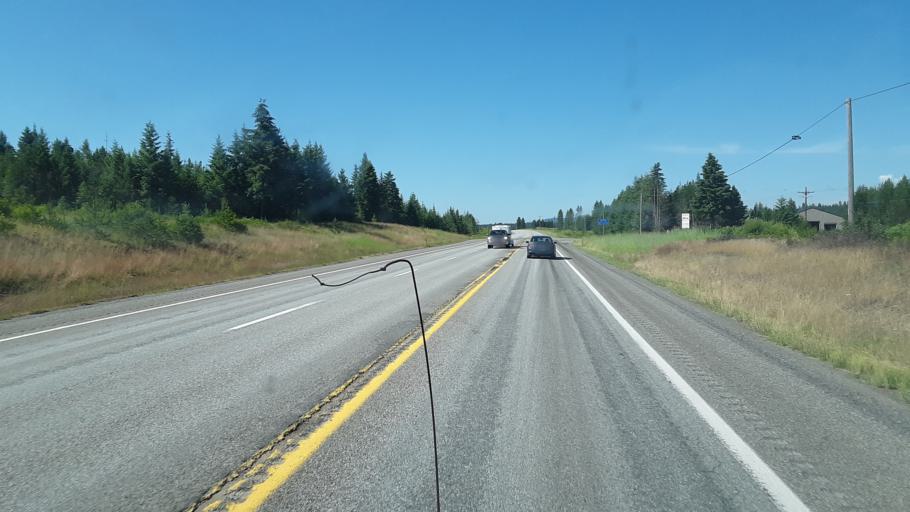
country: US
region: Idaho
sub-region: Kootenai County
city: Spirit Lake
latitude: 48.0071
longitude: -116.6683
